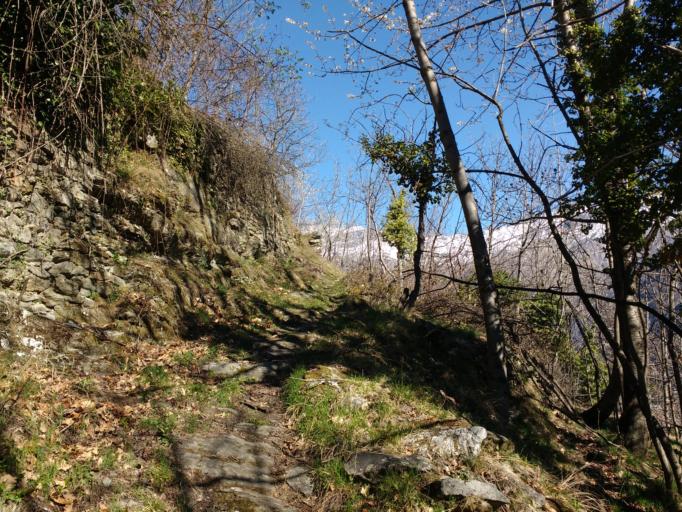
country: IT
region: Piedmont
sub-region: Provincia di Torino
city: Giaglione
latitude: 45.1454
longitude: 7.0103
